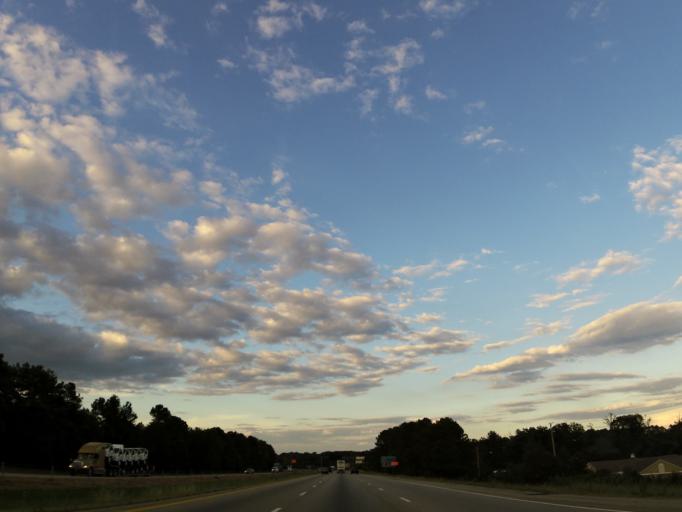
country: US
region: Tennessee
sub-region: Bradley County
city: Cleveland
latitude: 35.1953
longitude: -84.8838
